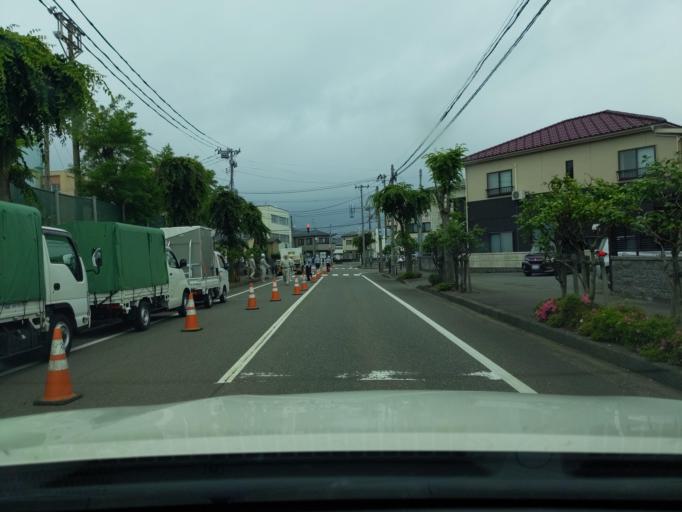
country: JP
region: Niigata
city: Kashiwazaki
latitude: 37.3732
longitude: 138.5579
